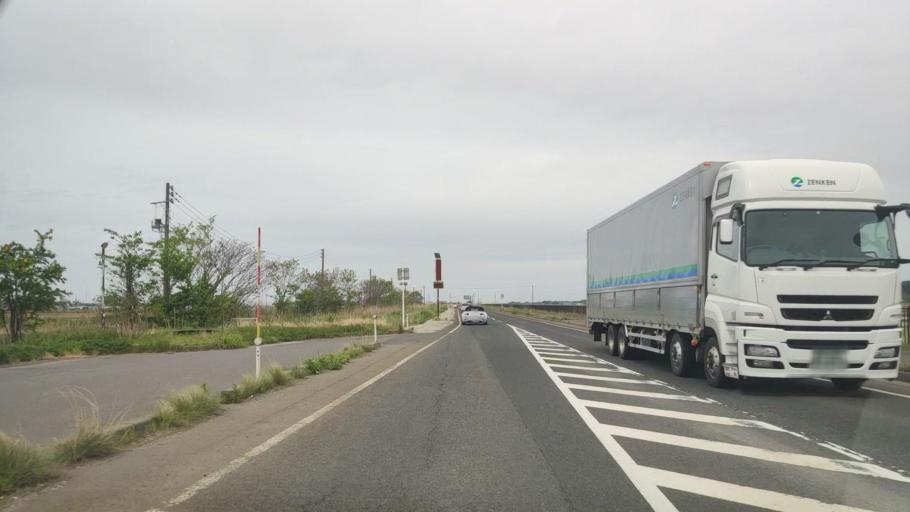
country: JP
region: Niigata
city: Niitsu-honcho
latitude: 37.7534
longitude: 139.0894
